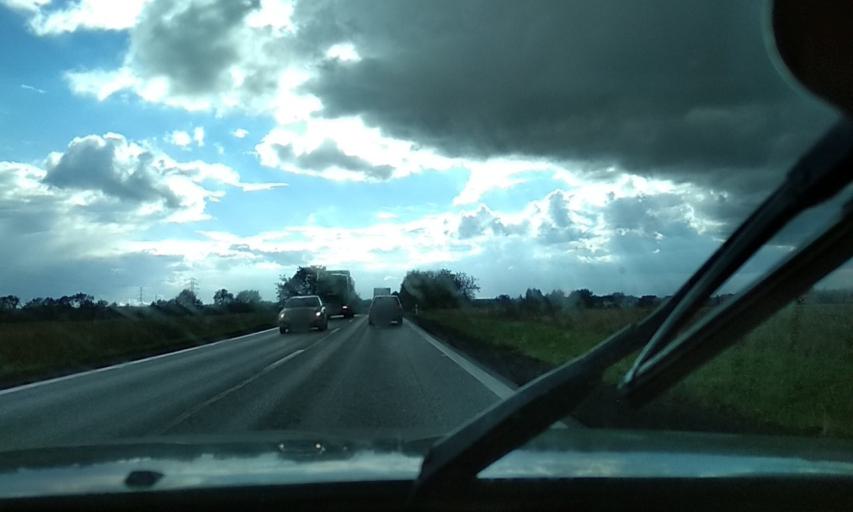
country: PL
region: Silesian Voivodeship
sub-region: Powiat gliwicki
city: Zernica
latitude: 50.2311
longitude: 18.6256
